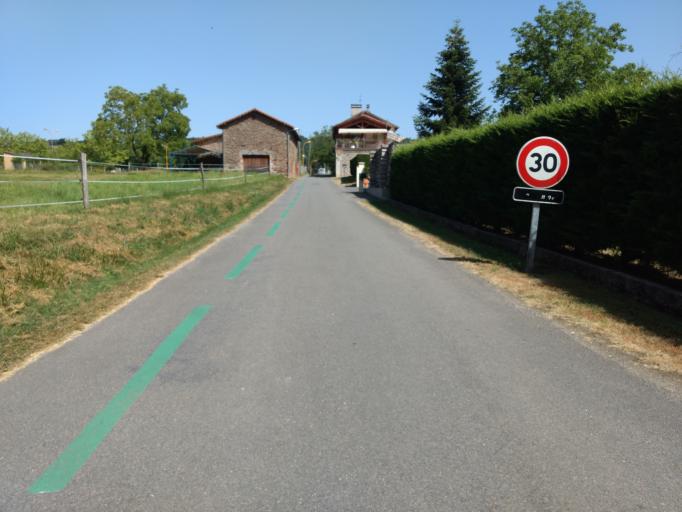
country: FR
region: Midi-Pyrenees
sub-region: Departement de l'Aveyron
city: Livinhac-le-Haut
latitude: 44.6086
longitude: 2.2339
